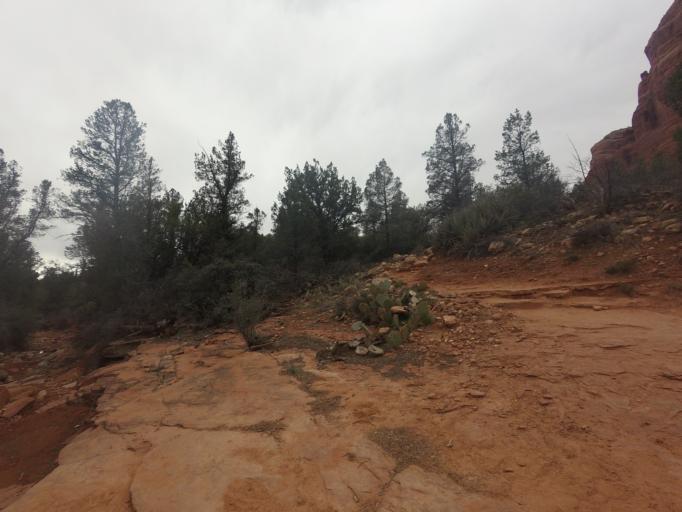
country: US
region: Arizona
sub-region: Yavapai County
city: Village of Oak Creek (Big Park)
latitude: 34.7983
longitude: -111.7482
